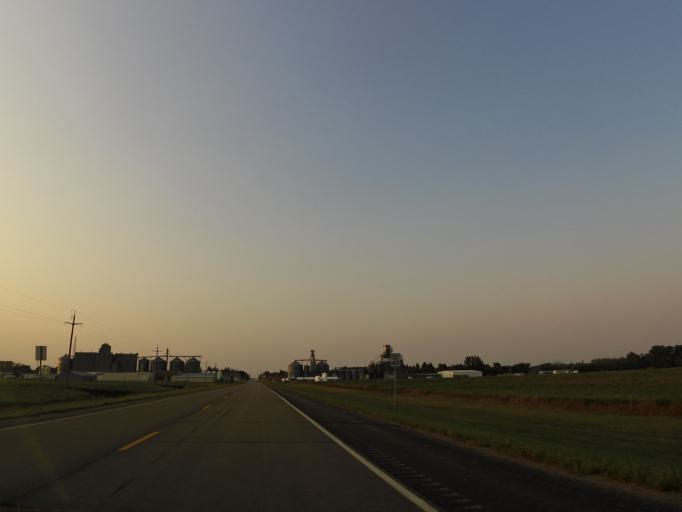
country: US
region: North Dakota
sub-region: Grand Forks County
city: Larimore
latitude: 47.8990
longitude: -97.6237
